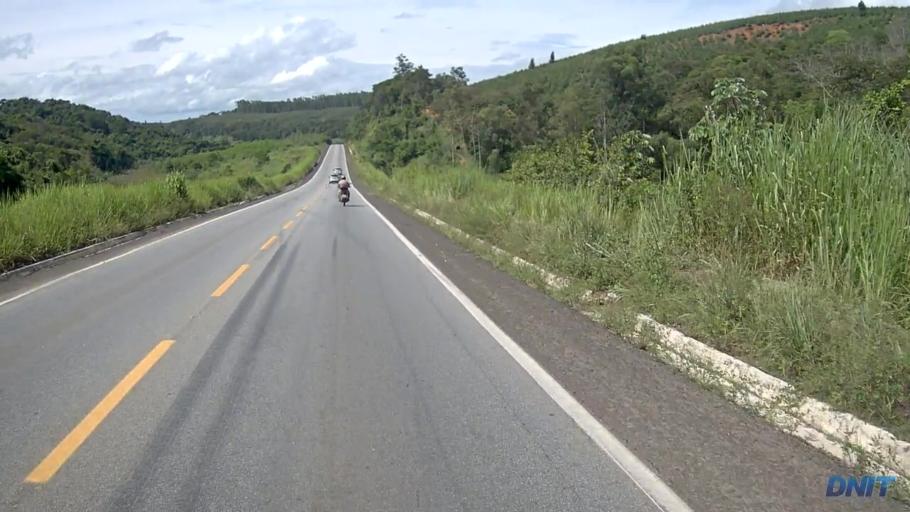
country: BR
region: Minas Gerais
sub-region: Ipaba
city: Ipaba
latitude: -19.4115
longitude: -42.4895
